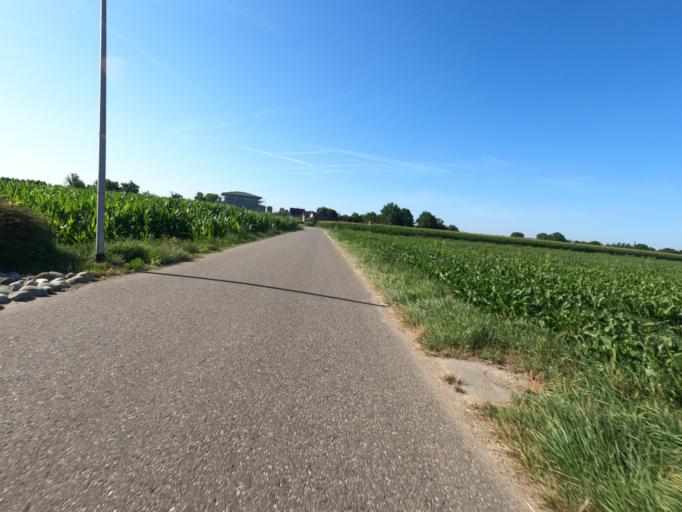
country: DE
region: North Rhine-Westphalia
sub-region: Regierungsbezirk Koln
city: Heinsberg
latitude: 51.0772
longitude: 6.1147
